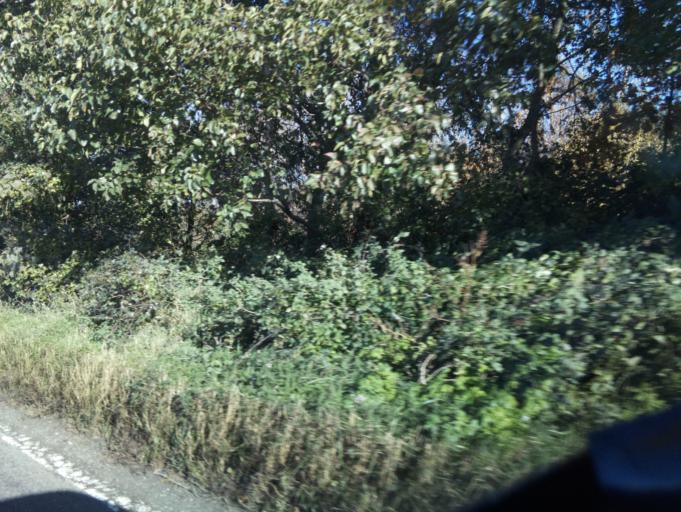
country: GB
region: England
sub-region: Somerset
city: Yeovil
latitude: 50.9005
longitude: -2.6205
